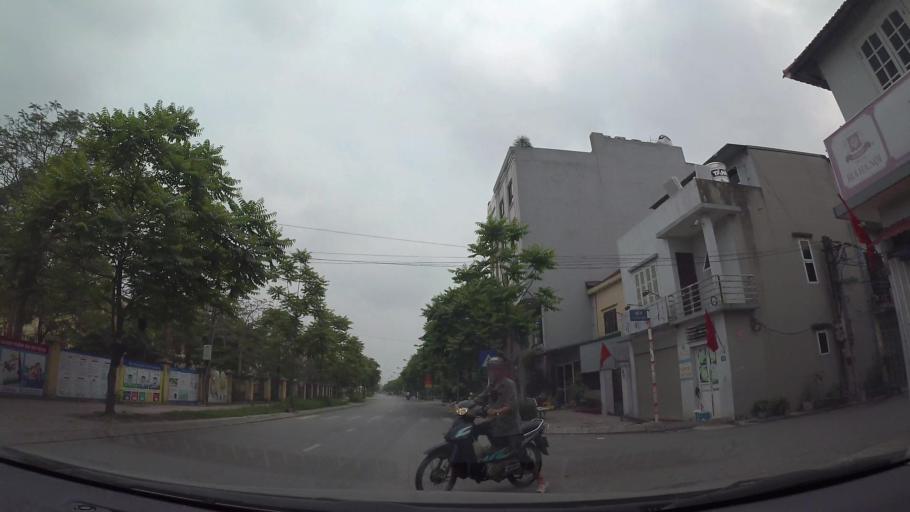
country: VN
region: Ha Noi
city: Trau Quy
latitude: 21.0604
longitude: 105.9007
